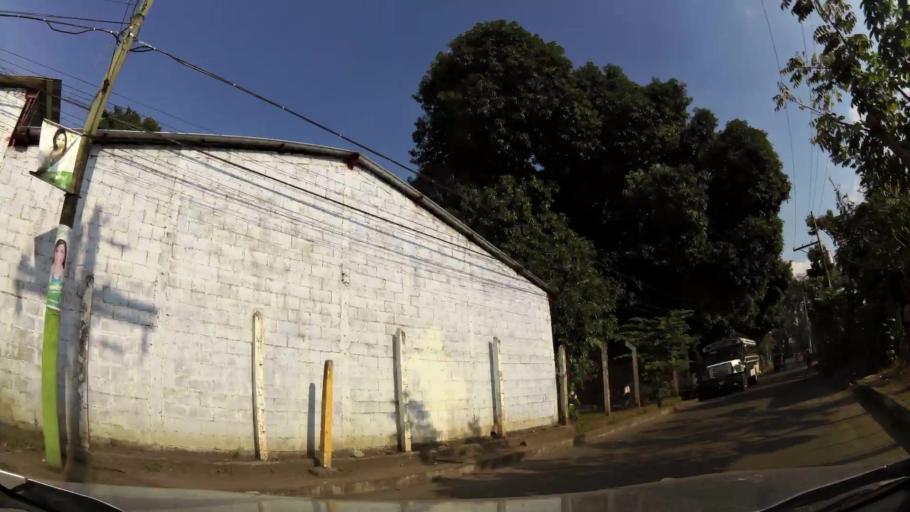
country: GT
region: Retalhuleu
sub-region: Municipio de Retalhuleu
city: Retalhuleu
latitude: 14.5290
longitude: -91.6885
